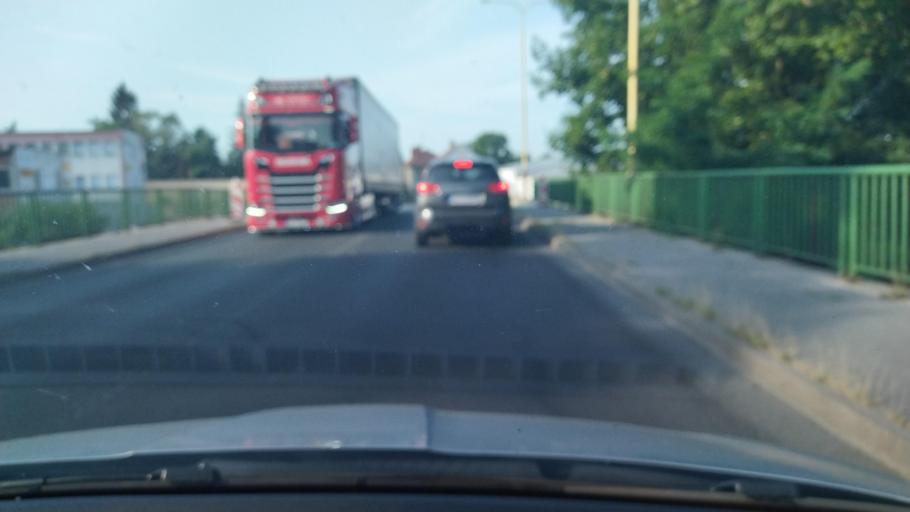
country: CZ
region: Liberecky
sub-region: Okres Ceska Lipa
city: Ceska Lipa
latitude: 50.6835
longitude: 14.5460
